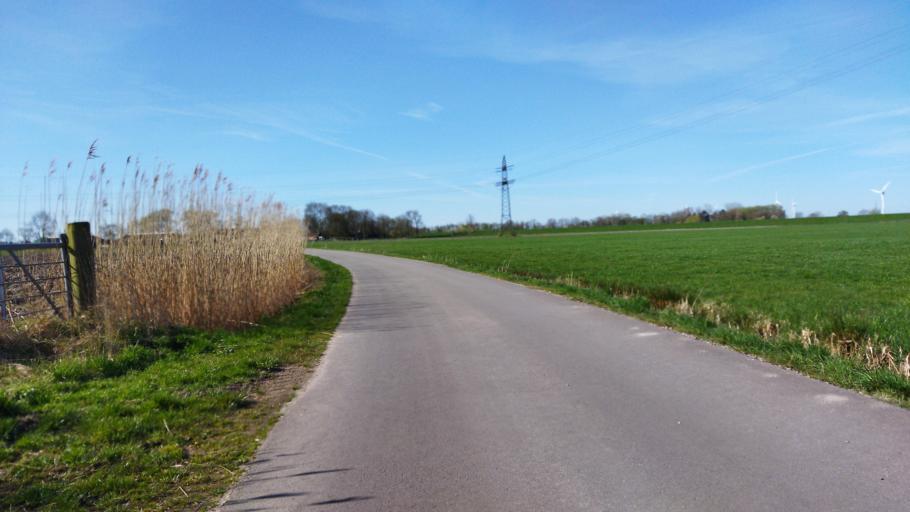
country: DE
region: Lower Saxony
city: Elsfleth
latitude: 53.2139
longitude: 8.4558
